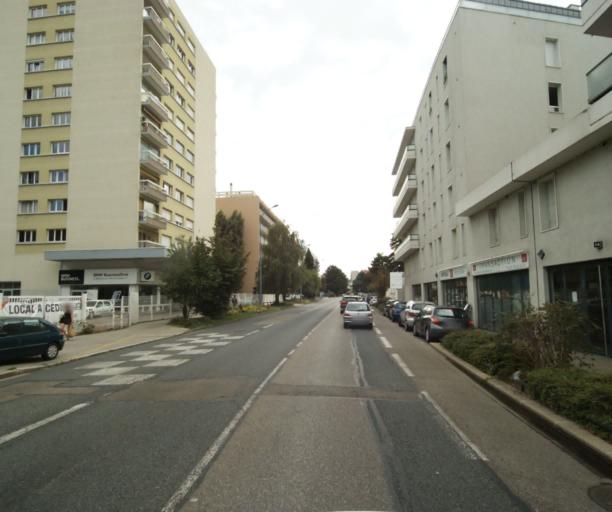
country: FR
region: Rhone-Alpes
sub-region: Departement de l'Isere
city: Grenoble
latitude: 45.1795
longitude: 5.7283
